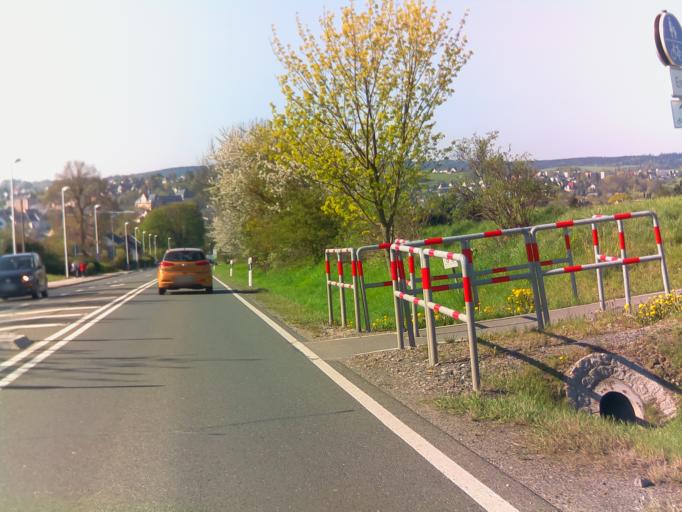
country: DE
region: Thuringia
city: Schleiz
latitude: 50.5881
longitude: 11.8120
